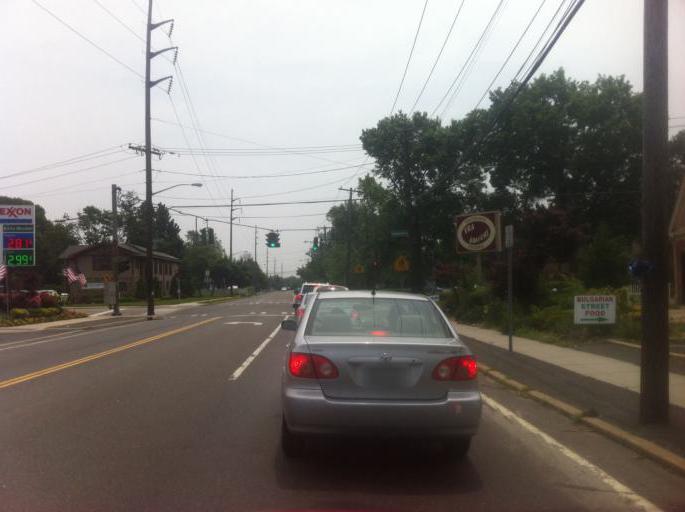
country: US
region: New York
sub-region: Nassau County
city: Plainedge
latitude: 40.7236
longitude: -73.4874
